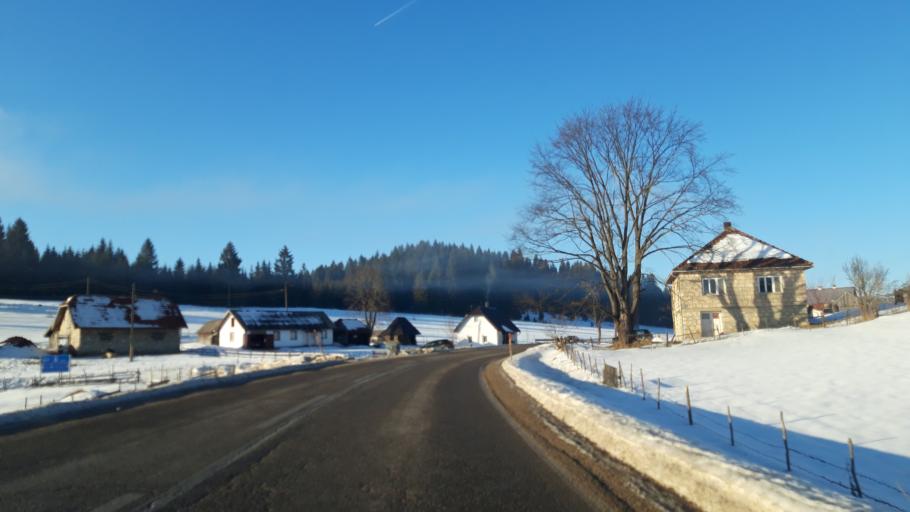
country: BA
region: Republika Srpska
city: Han Pijesak
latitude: 44.1093
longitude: 18.9687
